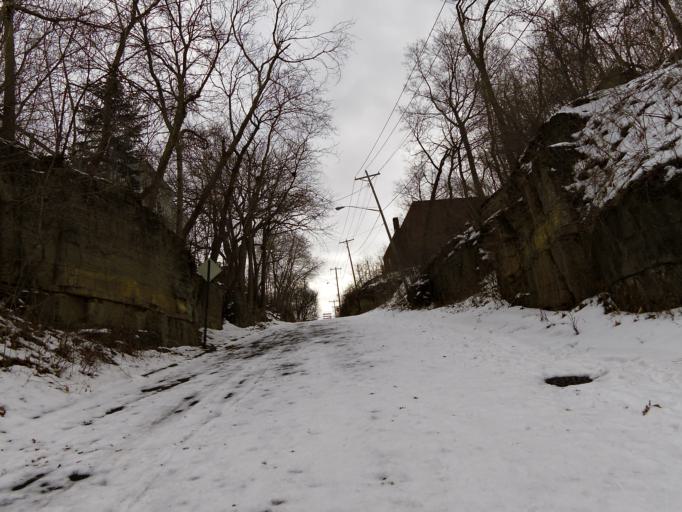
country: US
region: Minnesota
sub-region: Washington County
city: Stillwater
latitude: 45.0535
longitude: -92.8063
